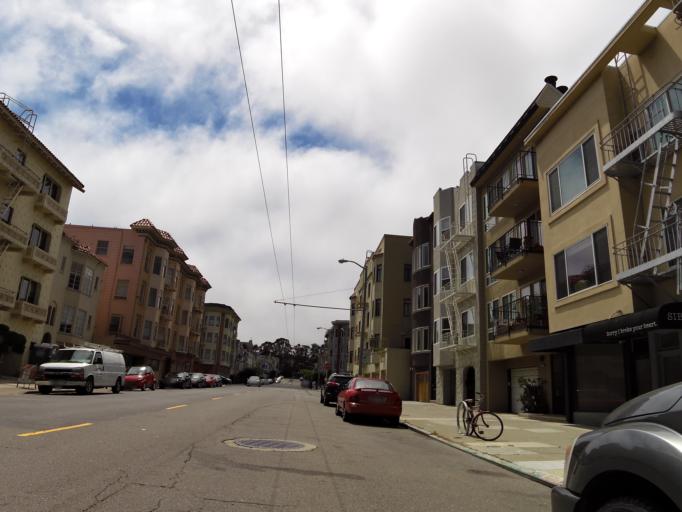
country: US
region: California
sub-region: San Francisco County
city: San Francisco
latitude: 37.7999
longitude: -122.4437
